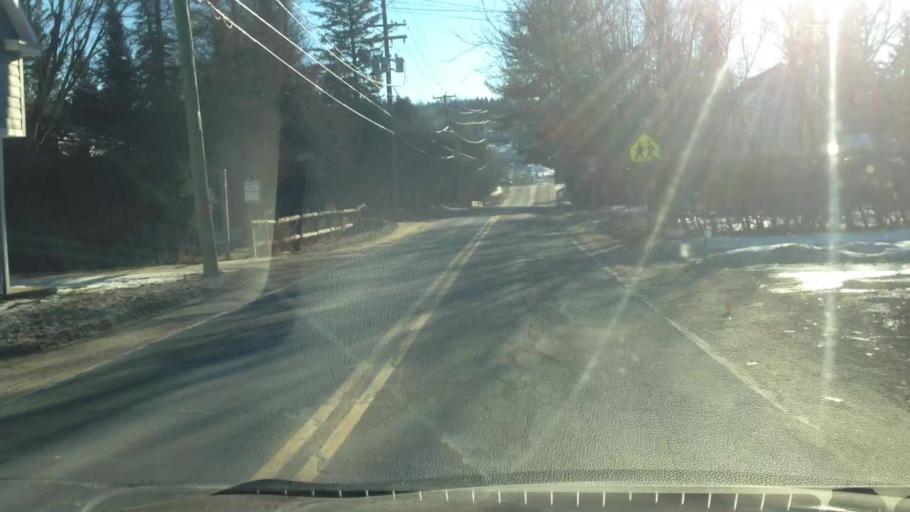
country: CA
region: Quebec
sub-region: Laurentides
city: Mont-Tremblant
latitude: 45.9694
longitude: -74.6157
